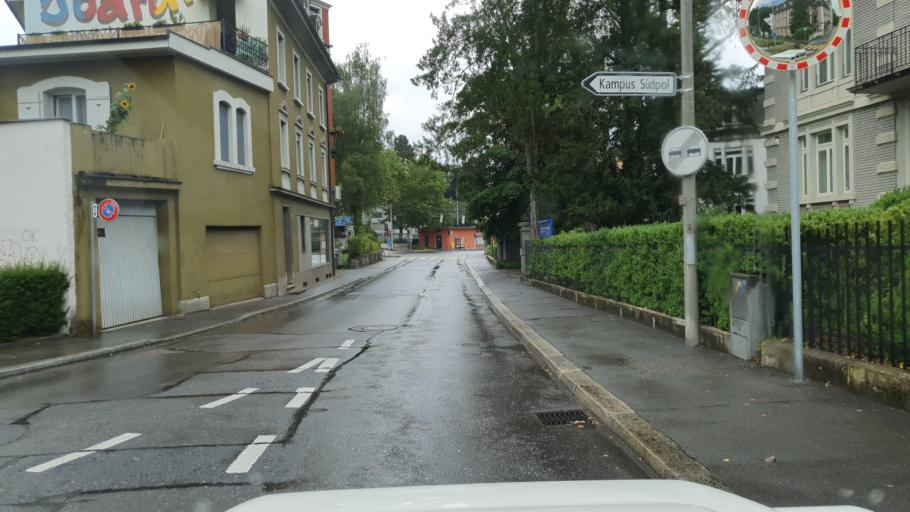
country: CH
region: Lucerne
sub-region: Lucerne-Stadt District
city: Luzern
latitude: 47.0390
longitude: 8.3009
